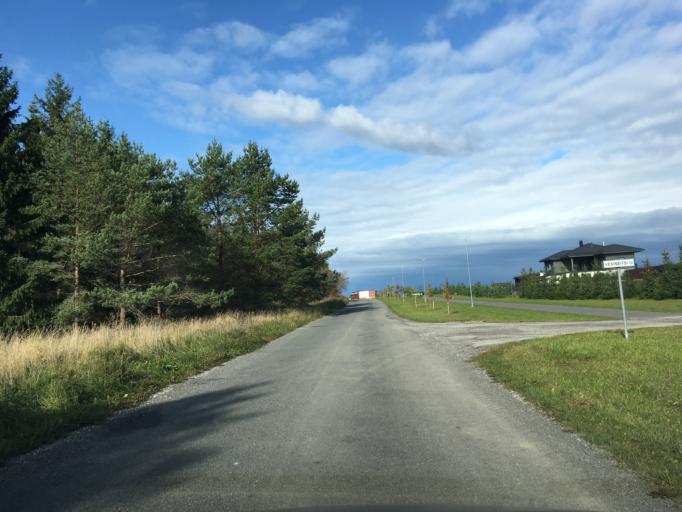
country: EE
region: Harju
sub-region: Saue vald
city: Laagri
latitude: 59.3429
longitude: 24.6486
